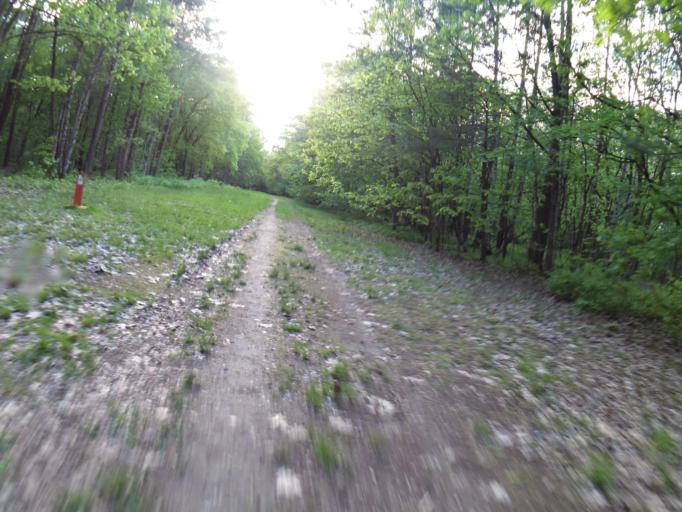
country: BE
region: Flanders
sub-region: Provincie Limburg
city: Zutendaal
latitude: 50.9409
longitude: 5.5671
